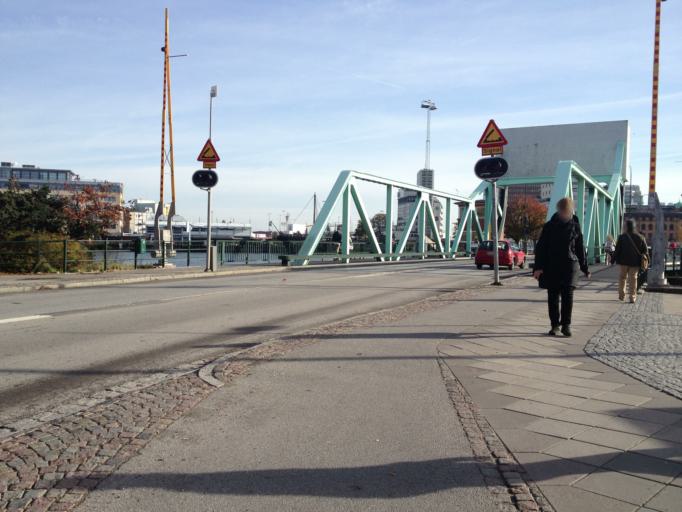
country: SE
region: Skane
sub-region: Malmo
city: Malmoe
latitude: 55.6127
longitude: 12.9930
